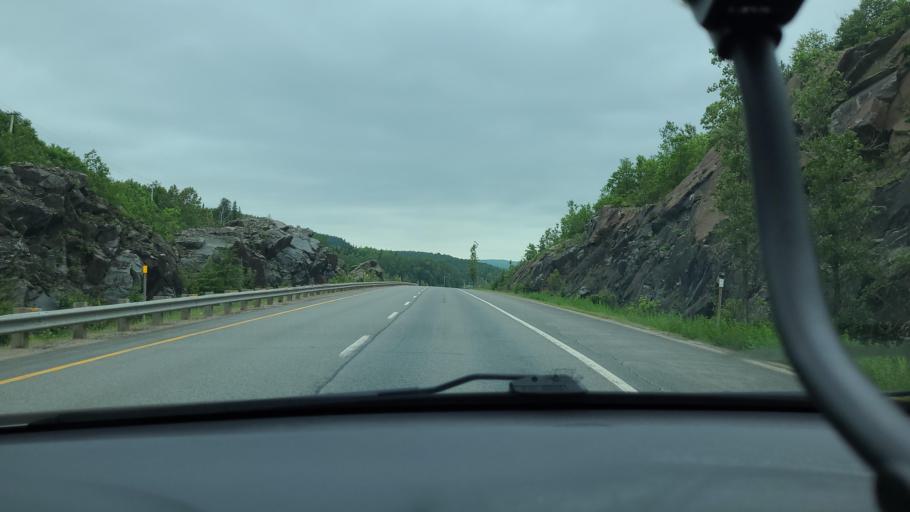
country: CA
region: Quebec
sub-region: Laurentides
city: Labelle
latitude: 46.1653
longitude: -74.7109
